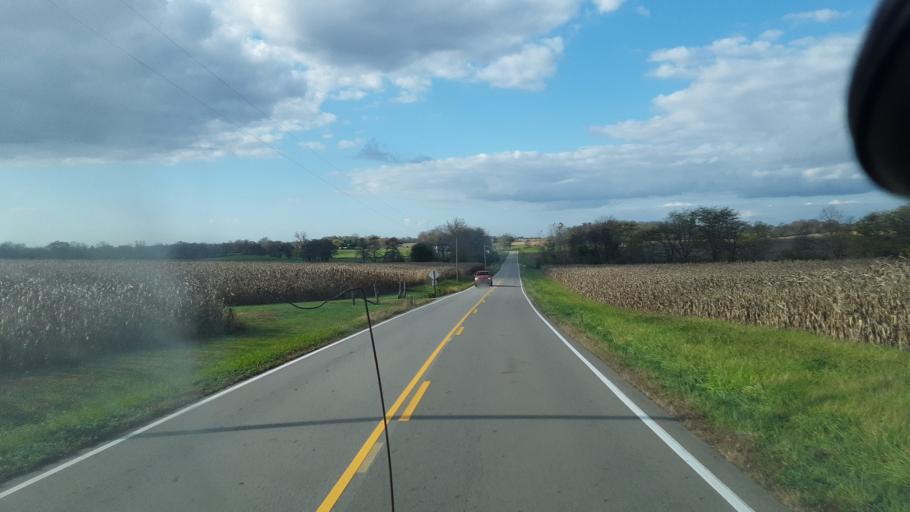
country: US
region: Ohio
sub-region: Highland County
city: Greenfield
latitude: 39.4213
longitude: -83.4450
